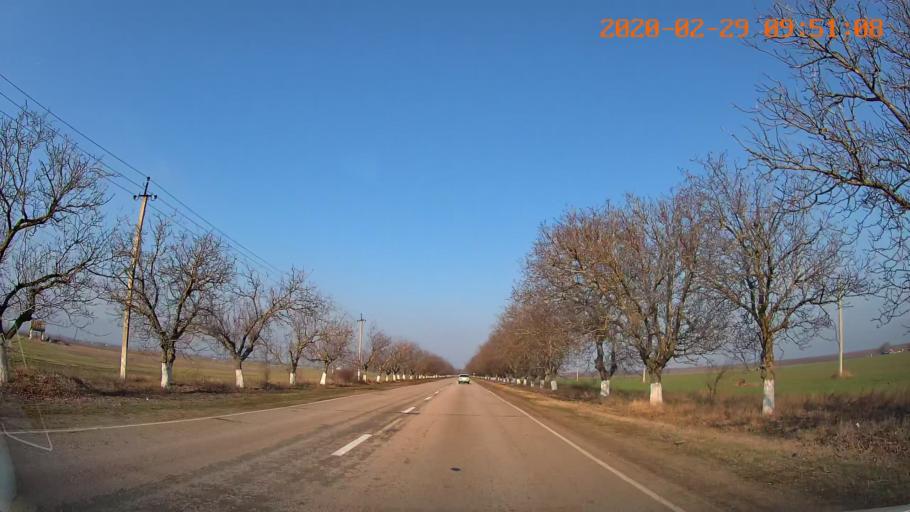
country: MD
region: Telenesti
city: Slobozia
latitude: 46.7061
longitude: 29.7443
